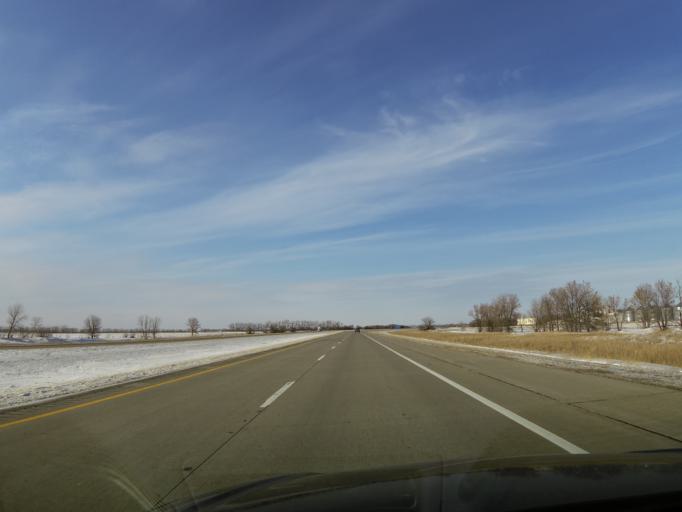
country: US
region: North Dakota
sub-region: Walsh County
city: Grafton
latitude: 48.4475
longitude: -97.1921
